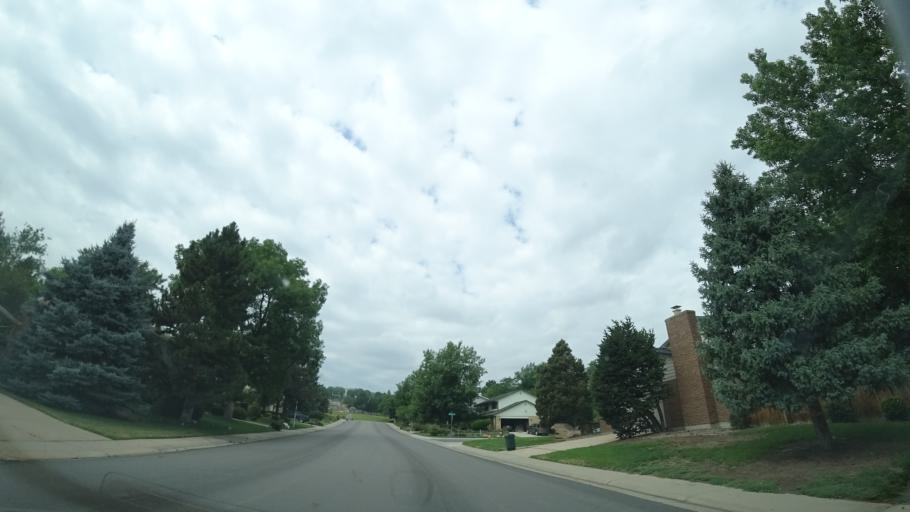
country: US
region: Colorado
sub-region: Jefferson County
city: West Pleasant View
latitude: 39.7207
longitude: -105.1570
